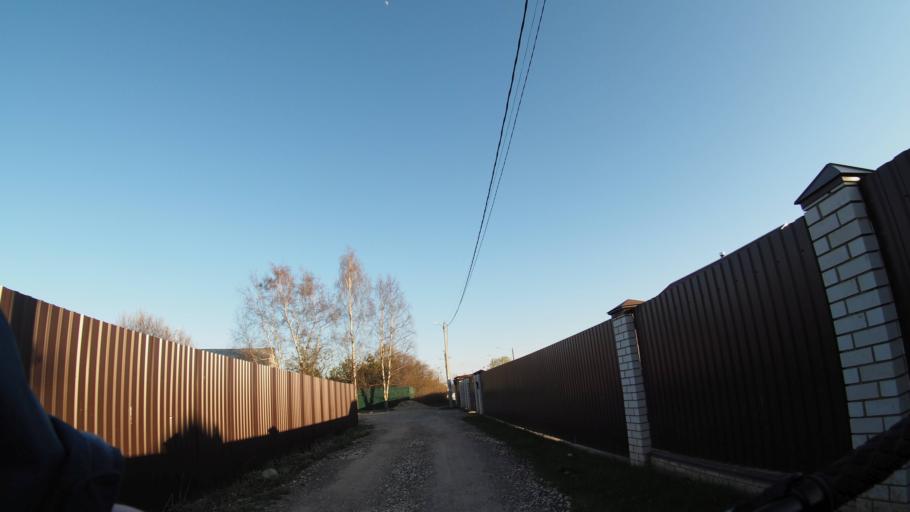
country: RU
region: Moskovskaya
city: Malyshevo
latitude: 55.4978
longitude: 38.3503
